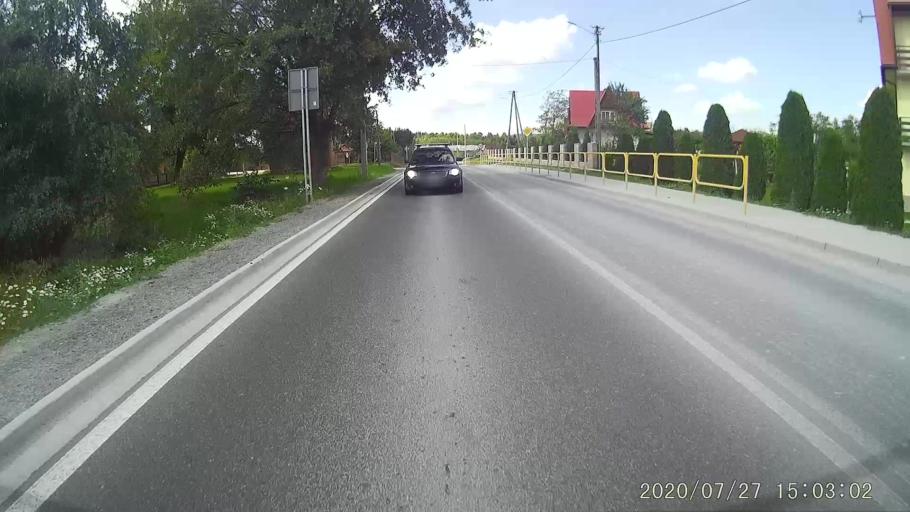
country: PL
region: Lesser Poland Voivodeship
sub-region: Powiat suski
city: Naprawa
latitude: 49.6688
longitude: 19.8918
